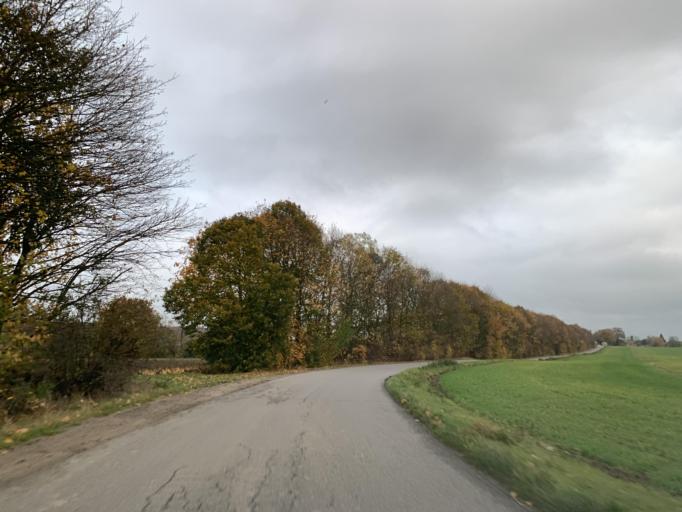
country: DE
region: Mecklenburg-Vorpommern
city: Gross Nemerow
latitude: 53.4726
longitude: 13.2683
